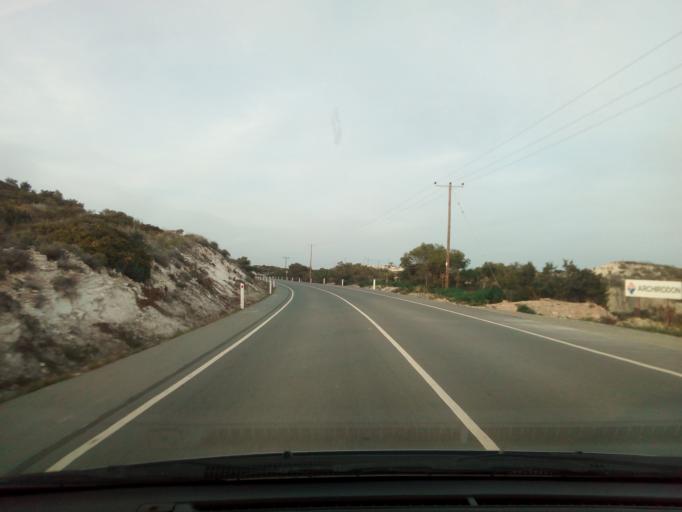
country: CY
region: Limassol
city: Pyrgos
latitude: 34.7241
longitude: 33.2744
